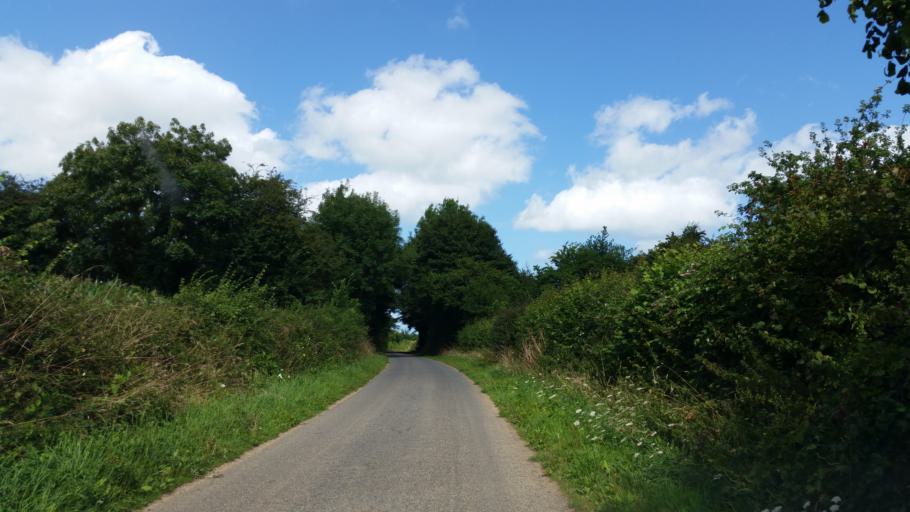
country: FR
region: Lower Normandy
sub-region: Departement de la Manche
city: Montebourg
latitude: 49.4620
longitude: -1.3392
